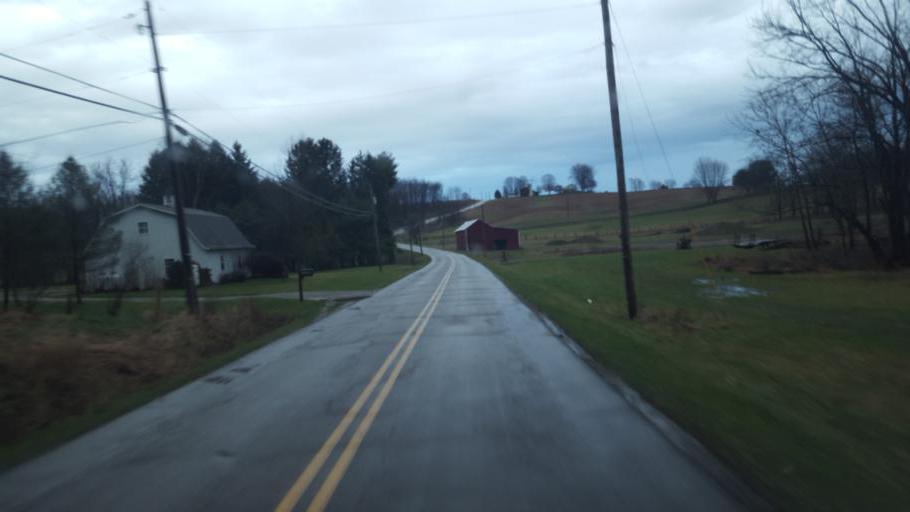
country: US
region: Ohio
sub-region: Knox County
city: Fredericktown
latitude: 40.4847
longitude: -82.5365
